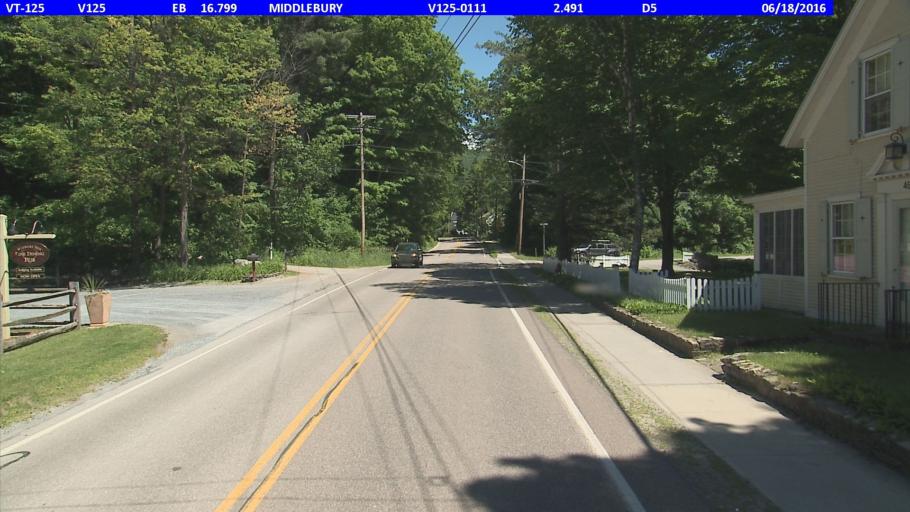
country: US
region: Vermont
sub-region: Addison County
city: Middlebury (village)
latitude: 43.9713
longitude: -73.0921
